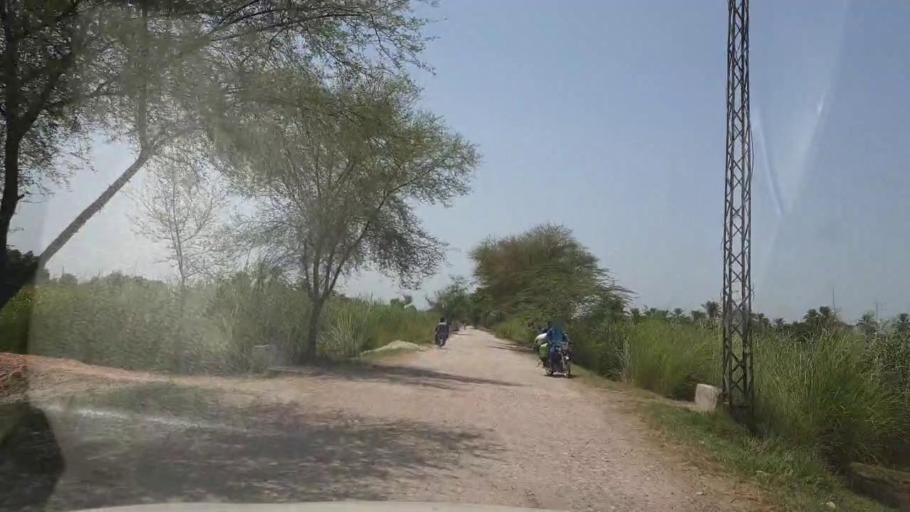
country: PK
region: Sindh
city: Bozdar
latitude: 27.1255
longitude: 68.6317
